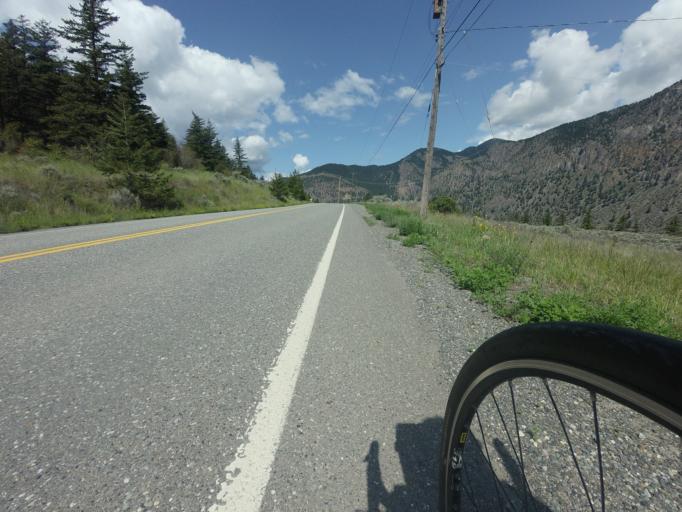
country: CA
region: British Columbia
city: Lillooet
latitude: 50.7574
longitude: -121.9005
